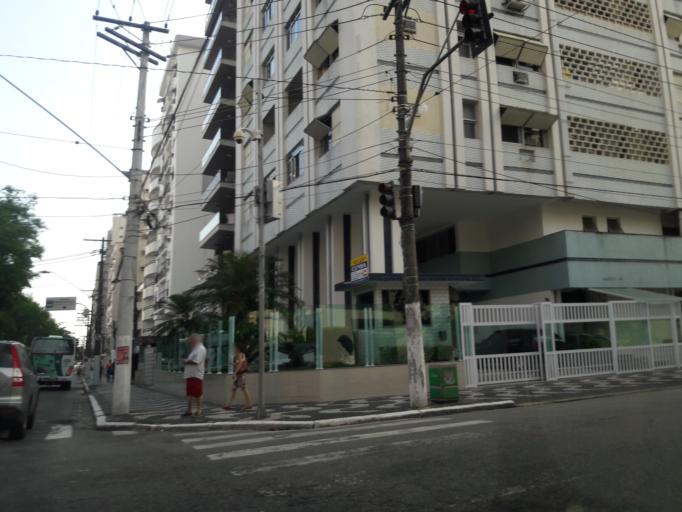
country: BR
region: Sao Paulo
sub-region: Santos
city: Santos
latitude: -23.9654
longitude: -46.3389
